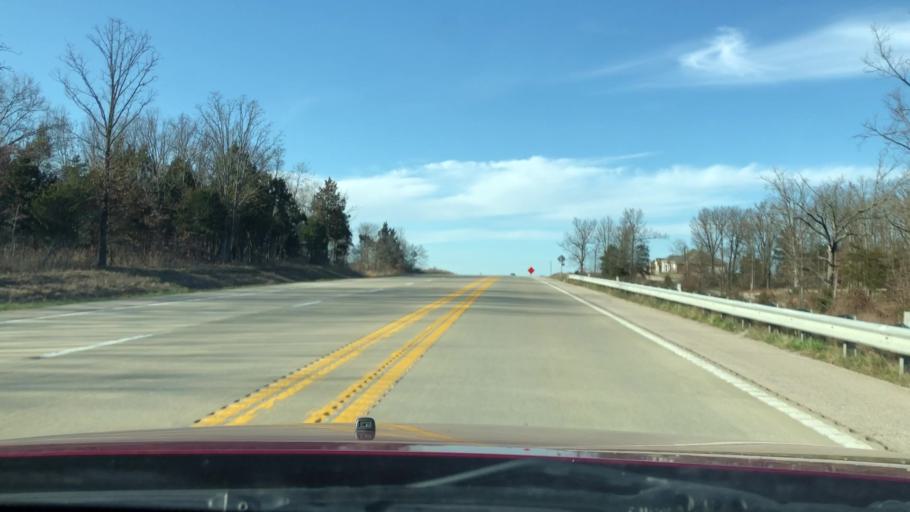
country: US
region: Missouri
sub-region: Camden County
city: Camdenton
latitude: 37.9460
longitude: -92.7156
